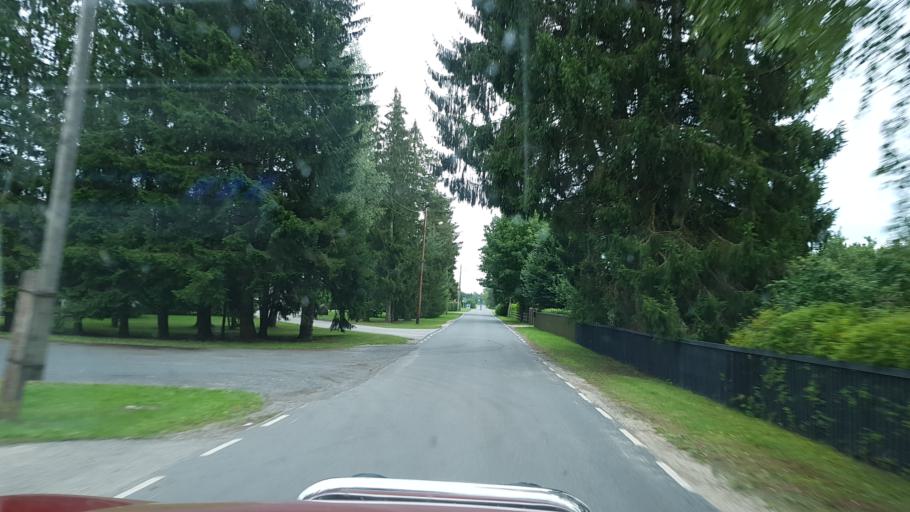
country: EE
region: Harju
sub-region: Nissi vald
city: Turba
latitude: 58.8798
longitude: 24.0765
